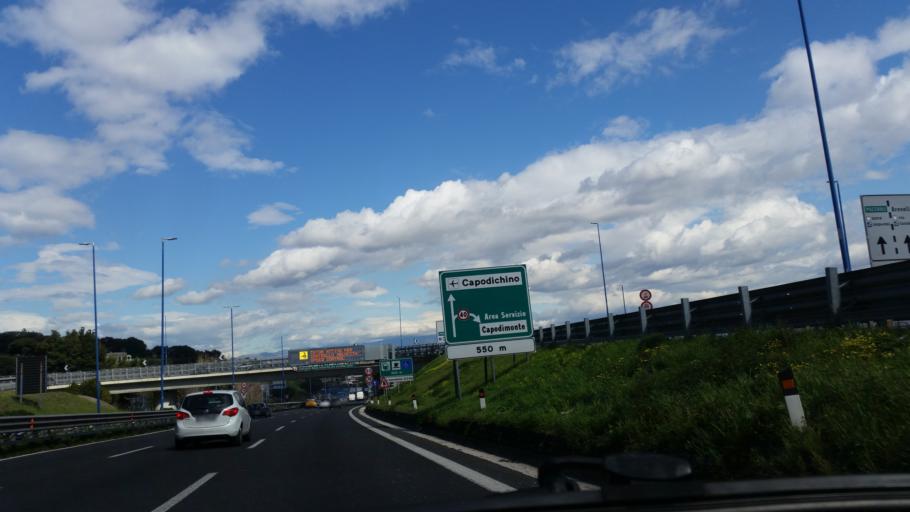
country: IT
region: Campania
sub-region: Provincia di Napoli
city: Napoli
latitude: 40.8618
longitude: 14.2339
